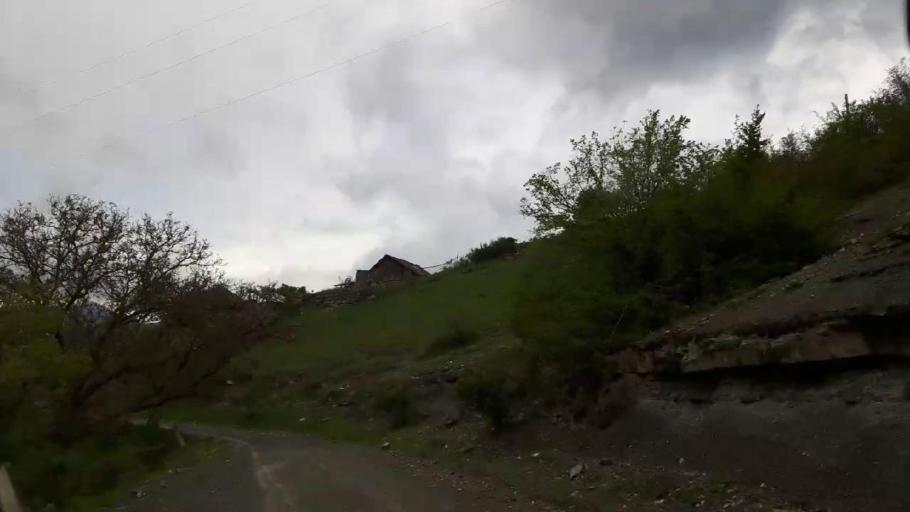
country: GE
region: Shida Kartli
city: Gori
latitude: 41.8655
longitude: 43.9812
